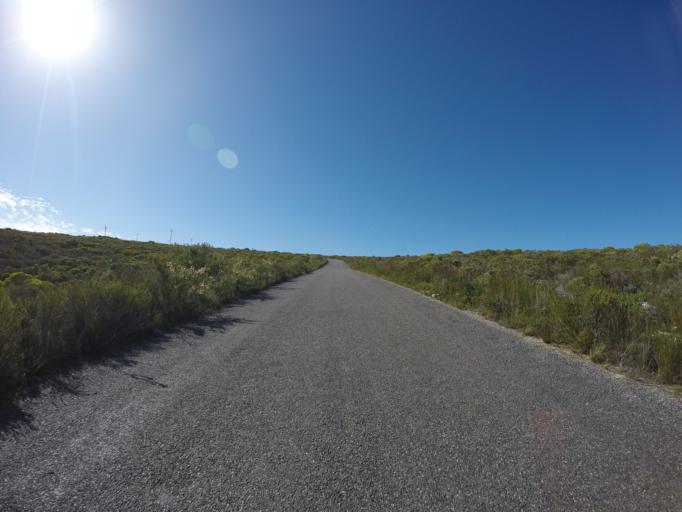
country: ZA
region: Western Cape
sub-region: Overberg District Municipality
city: Bredasdorp
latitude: -34.4257
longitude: 20.4140
